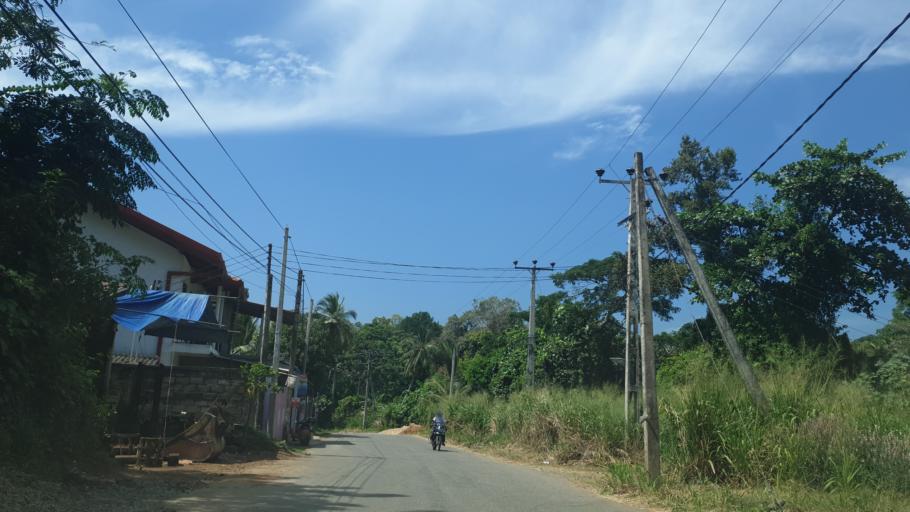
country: LK
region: Southern
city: Matara
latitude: 5.9758
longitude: 80.6587
